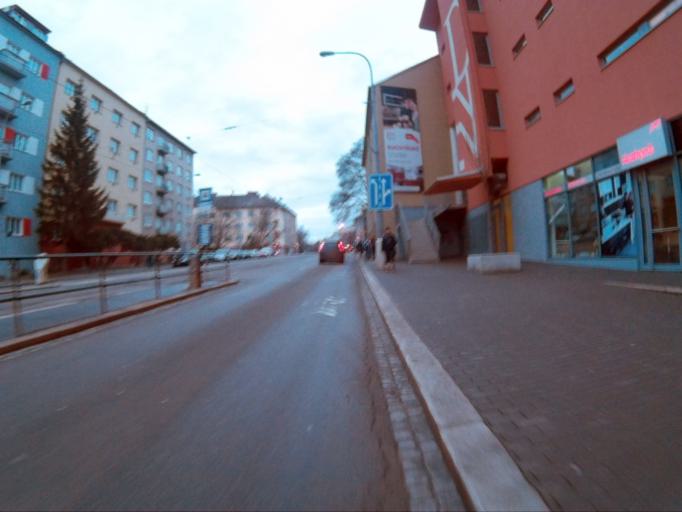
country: CZ
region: South Moravian
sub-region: Mesto Brno
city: Brno
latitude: 49.1838
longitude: 16.5950
